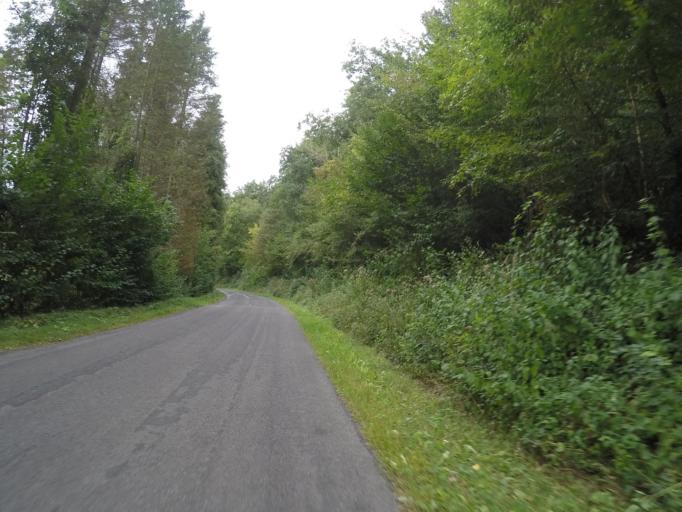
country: BE
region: Wallonia
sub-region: Province de Namur
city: Dinant
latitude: 50.2723
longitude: 4.9785
